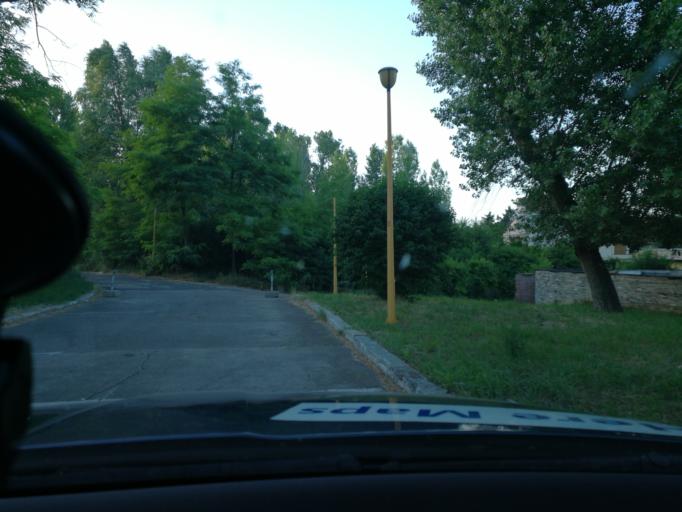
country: RO
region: Constanta
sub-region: Comuna Douazeci si Trei August
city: Douazeci si Trei August
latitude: 43.8694
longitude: 28.5978
